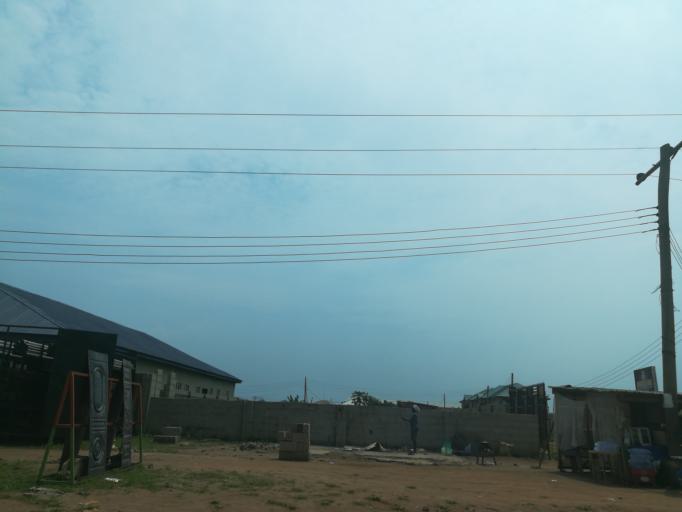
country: NG
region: Lagos
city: Ikorodu
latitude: 6.6055
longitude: 3.5989
